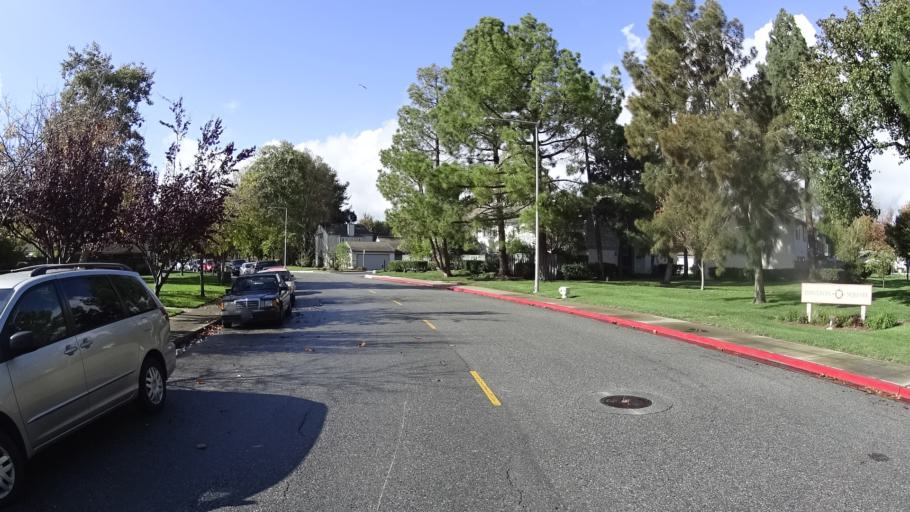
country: US
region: California
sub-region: San Mateo County
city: Foster City
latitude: 37.5490
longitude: -122.2665
